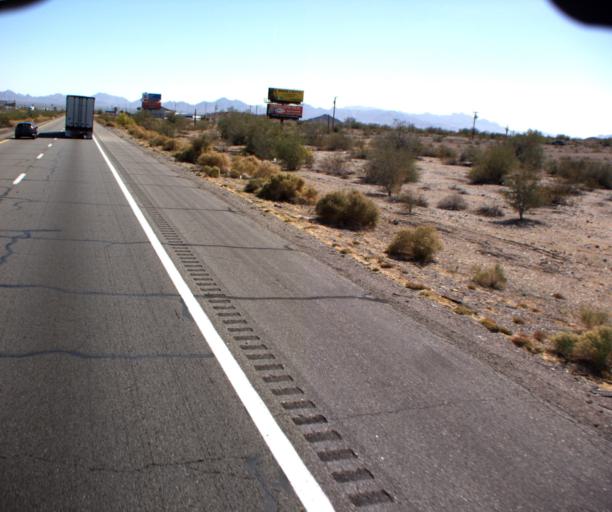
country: US
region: Arizona
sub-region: La Paz County
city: Quartzsite
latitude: 33.6572
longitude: -114.2579
